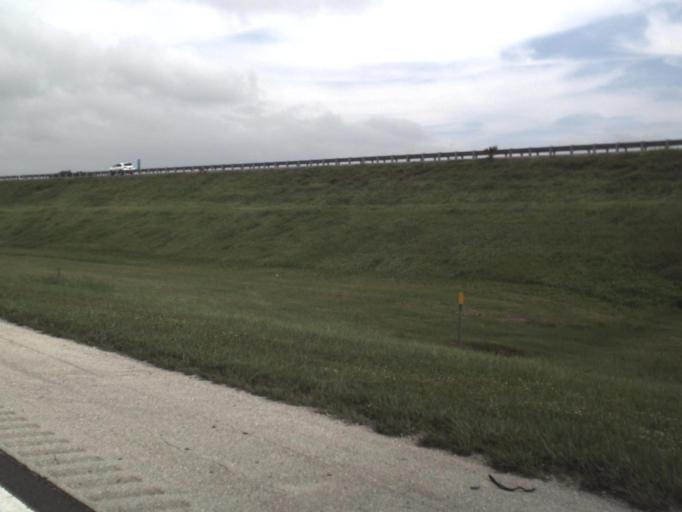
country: US
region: Florida
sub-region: Manatee County
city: Ellenton
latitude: 27.5804
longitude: -82.5144
